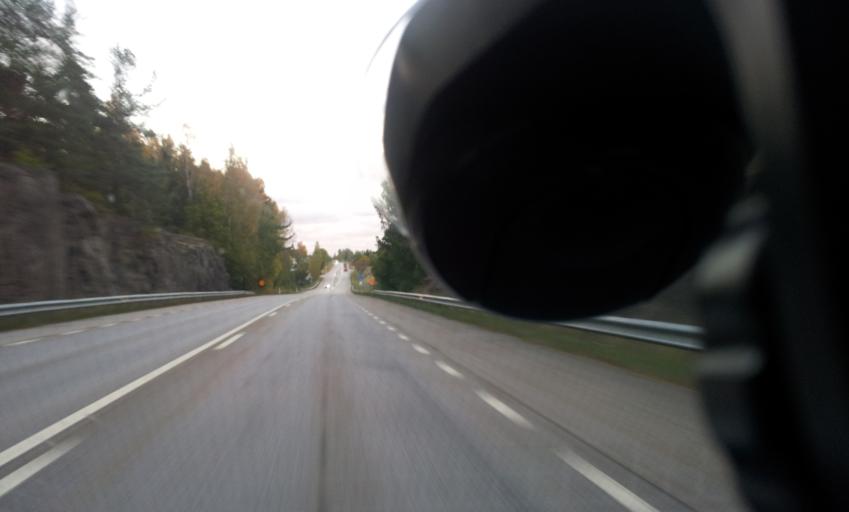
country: SE
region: Kalmar
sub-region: Vasterviks Kommun
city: Ankarsrum
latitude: 57.7057
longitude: 16.4456
